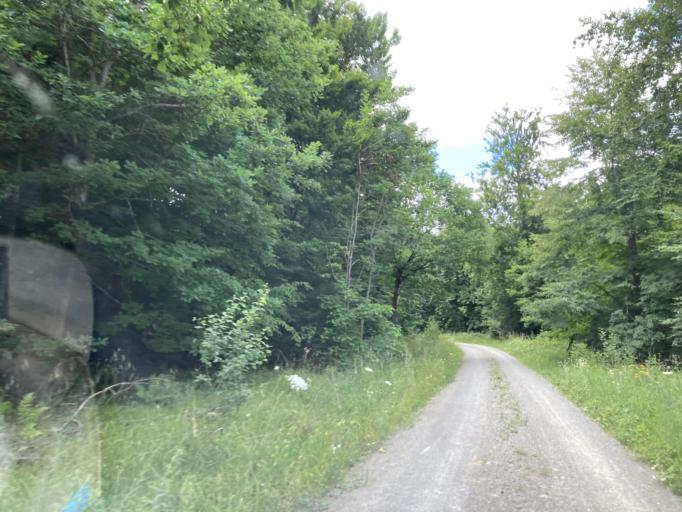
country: DE
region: Baden-Wuerttemberg
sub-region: Tuebingen Region
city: Ofterdingen
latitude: 48.4426
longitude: 9.0144
